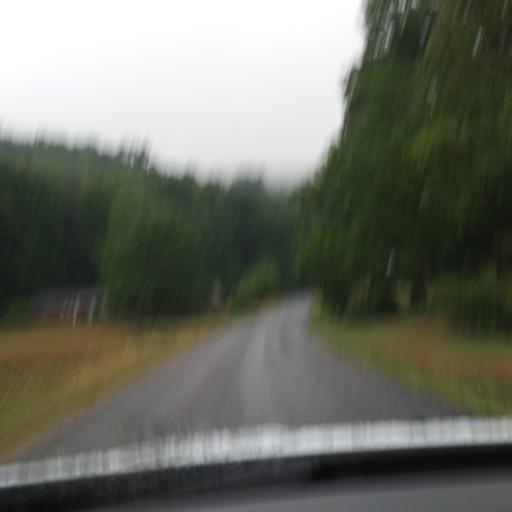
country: US
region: North Carolina
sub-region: Yancey County
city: Burnsville
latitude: 35.8798
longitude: -82.2989
